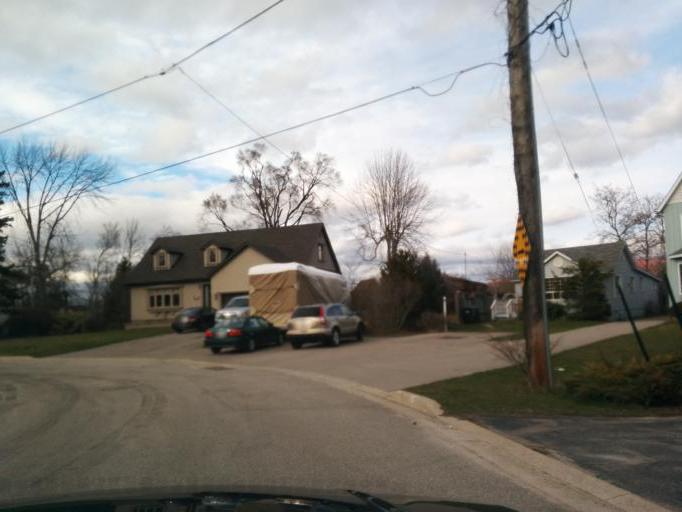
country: CA
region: Ontario
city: Etobicoke
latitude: 43.5690
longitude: -79.5627
